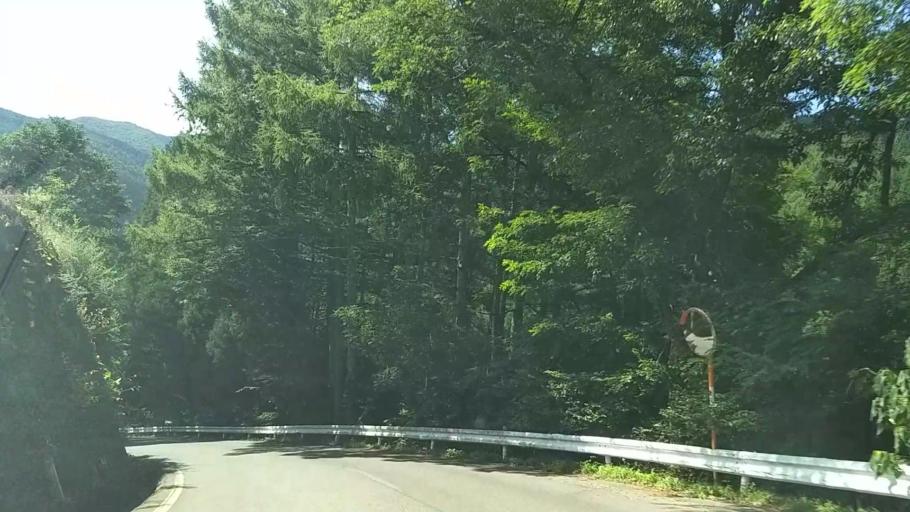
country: JP
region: Nagano
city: Matsumoto
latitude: 36.1990
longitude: 138.0652
